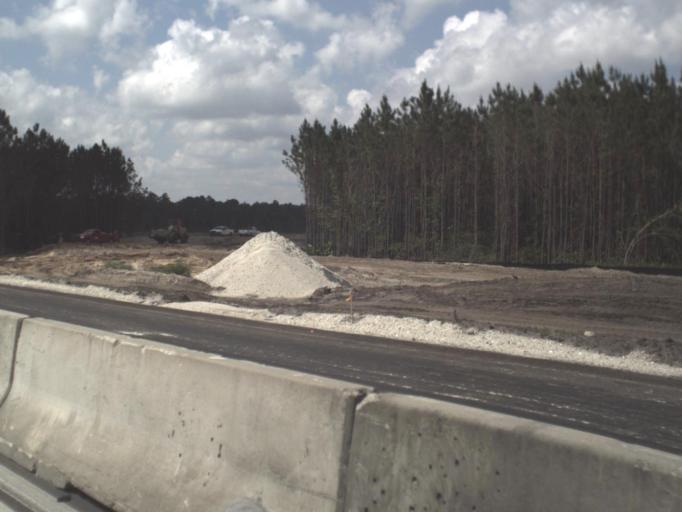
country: US
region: Florida
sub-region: Saint Johns County
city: Fruit Cove
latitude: 30.1168
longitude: -81.5161
